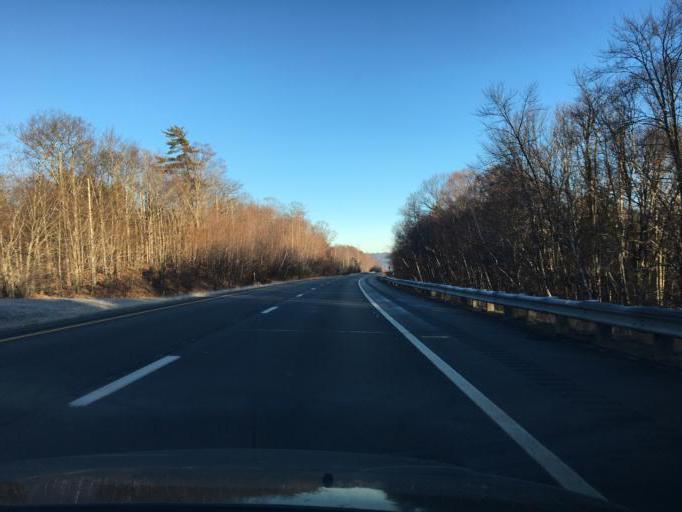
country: US
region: New Hampshire
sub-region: Belknap County
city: Sanbornton
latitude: 43.5486
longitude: -71.6163
